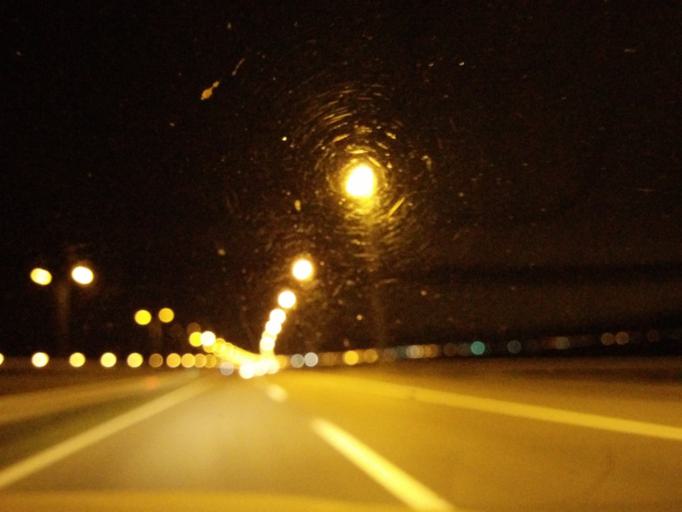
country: RS
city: Dobanovci
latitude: 44.8378
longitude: 20.2395
